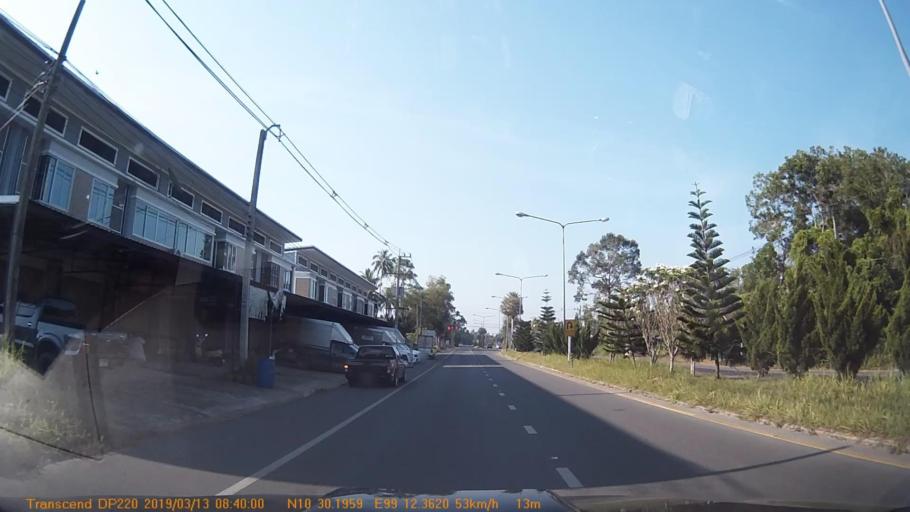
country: TH
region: Chumphon
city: Chumphon
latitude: 10.5031
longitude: 99.2060
